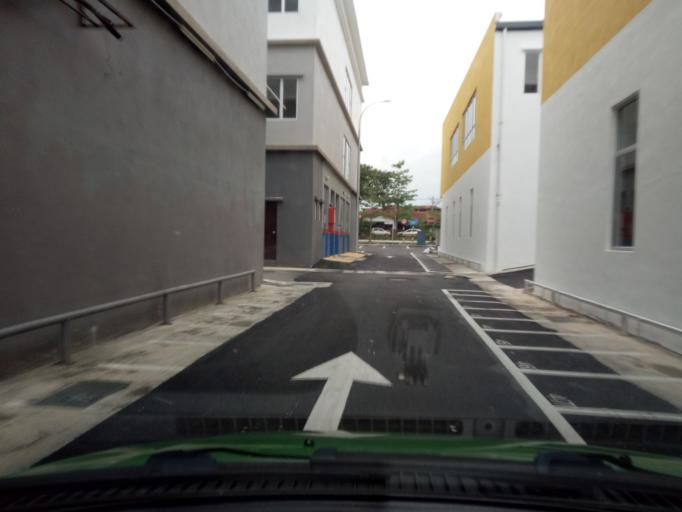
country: MY
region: Selangor
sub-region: Hulu Langat
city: Semenyih
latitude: 2.9264
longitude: 101.8601
